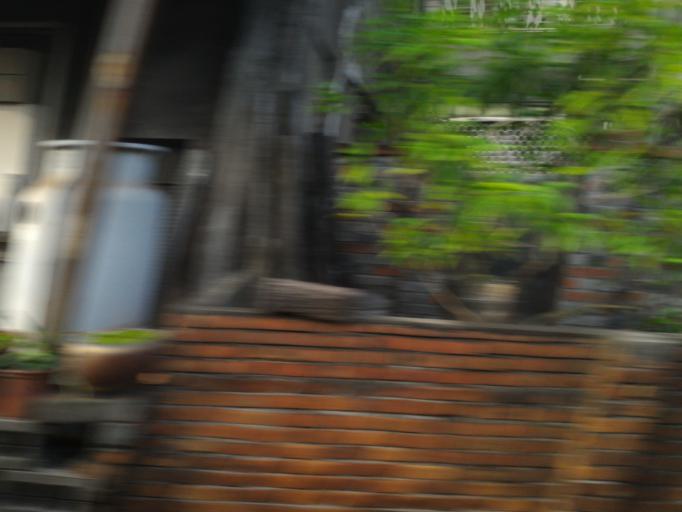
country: TW
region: Taiwan
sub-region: Taoyuan
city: Taoyuan
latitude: 24.9505
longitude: 121.3487
